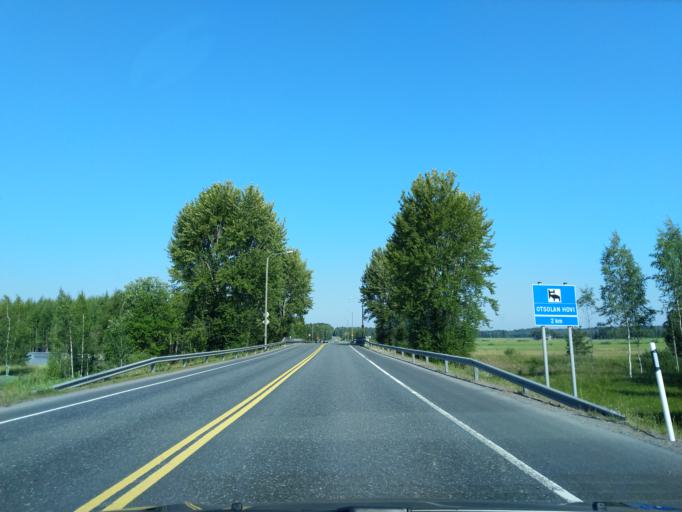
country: FI
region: Haeme
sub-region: Forssa
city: Humppila
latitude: 60.9529
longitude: 23.3407
